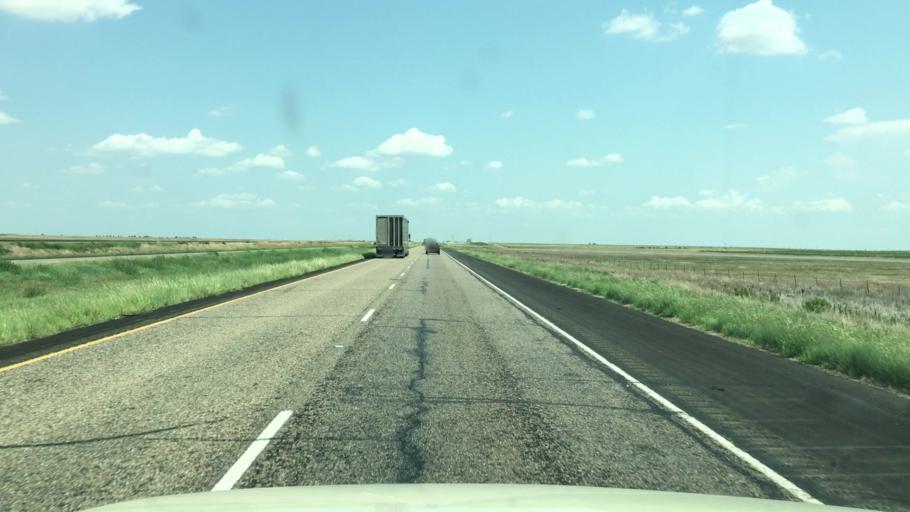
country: US
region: Texas
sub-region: Armstrong County
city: Claude
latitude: 35.1331
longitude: -101.4230
